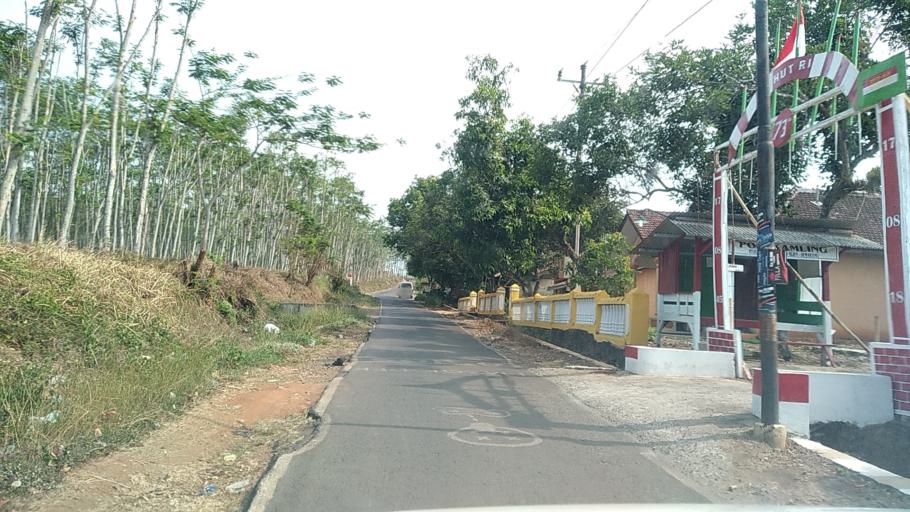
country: ID
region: Central Java
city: Semarang
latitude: -7.0315
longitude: 110.3145
